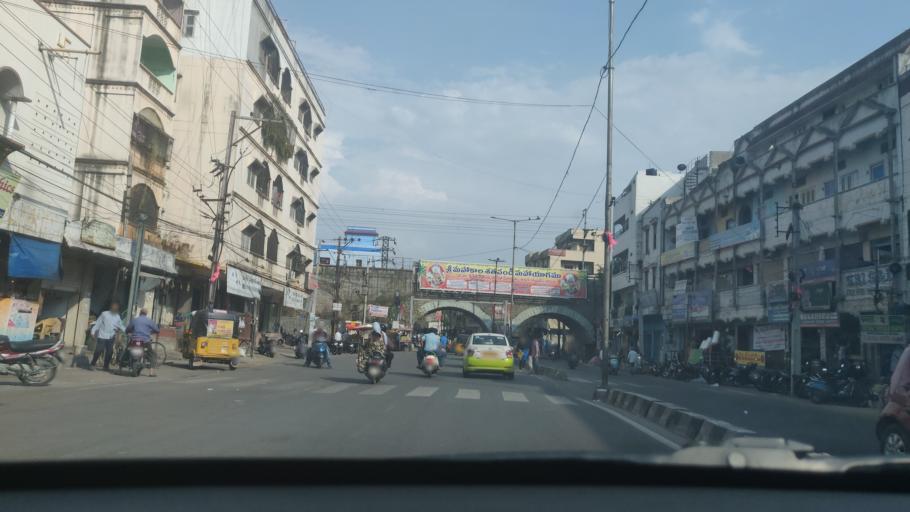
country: IN
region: Telangana
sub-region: Rangareddi
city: Gaddi Annaram
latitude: 17.3954
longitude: 78.5041
